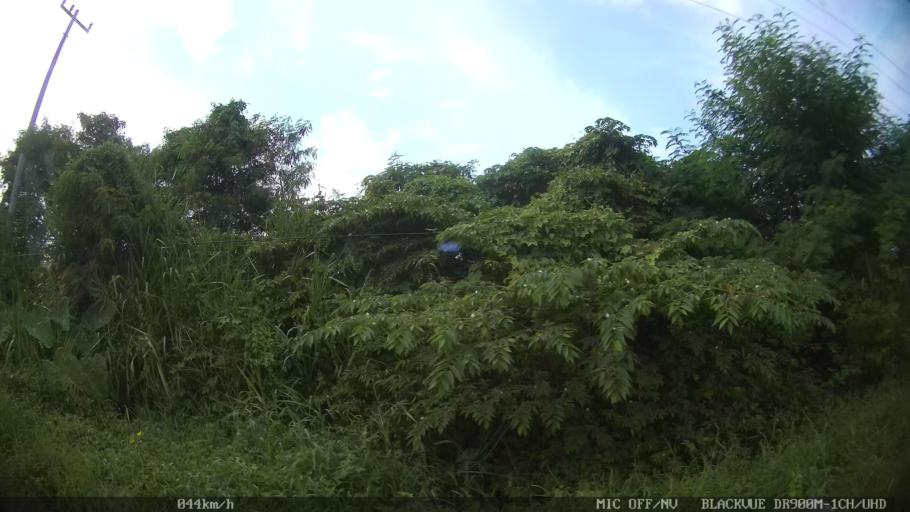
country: ID
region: North Sumatra
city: Medan
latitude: 3.6057
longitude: 98.7324
